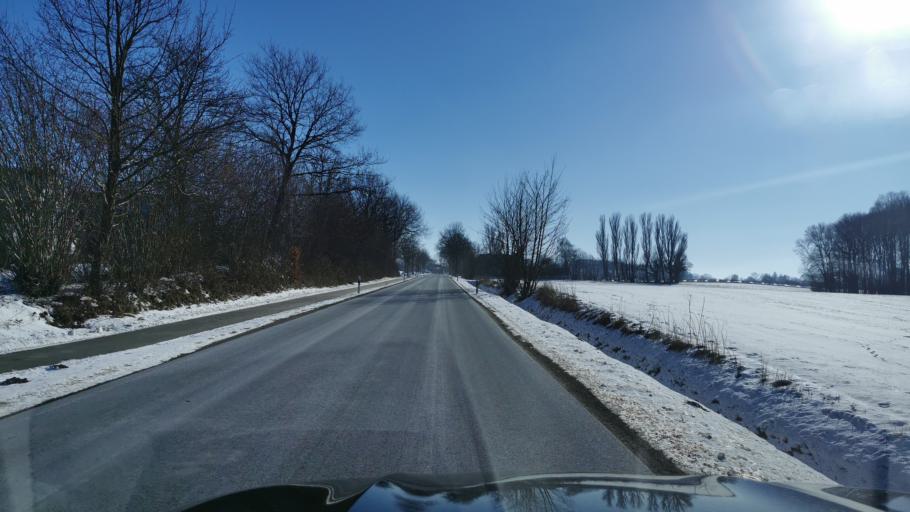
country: DE
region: Schleswig-Holstein
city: Langballig
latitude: 54.7940
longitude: 9.6385
